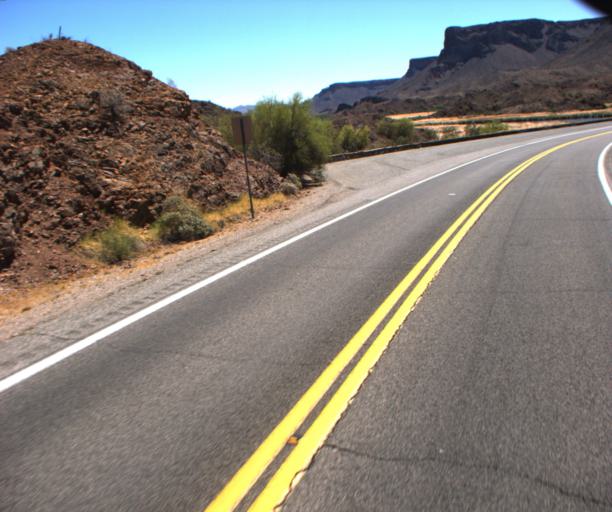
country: US
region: Arizona
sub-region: La Paz County
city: Cienega Springs
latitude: 34.3030
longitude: -114.0938
